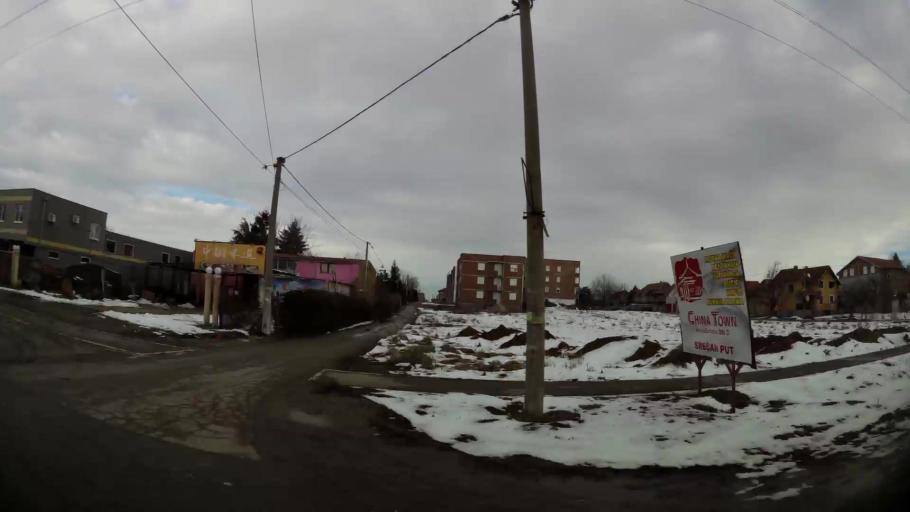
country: RS
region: Central Serbia
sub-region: Belgrade
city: Surcin
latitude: 44.7989
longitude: 20.3222
